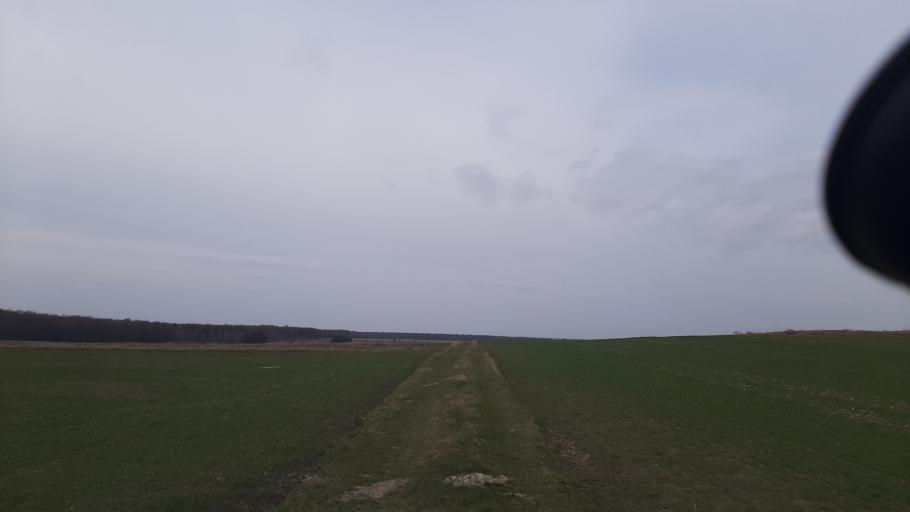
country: PL
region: Lublin Voivodeship
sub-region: Powiat lubelski
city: Jastkow
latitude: 51.3717
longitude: 22.4215
